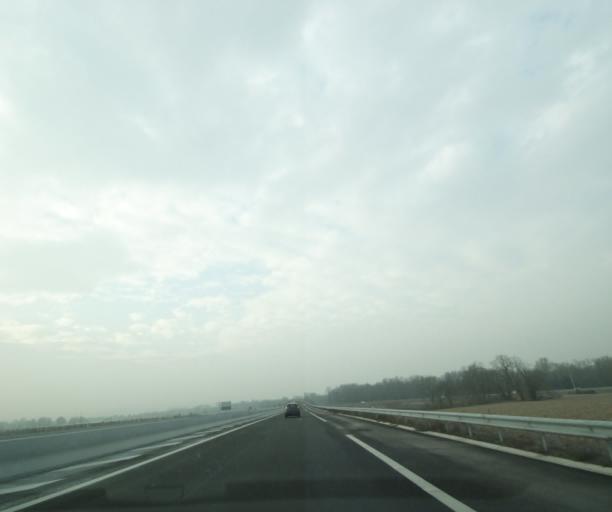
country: FR
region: Rhone-Alpes
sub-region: Departement du Rhone
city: Les Cheres
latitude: 45.9009
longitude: 4.7333
